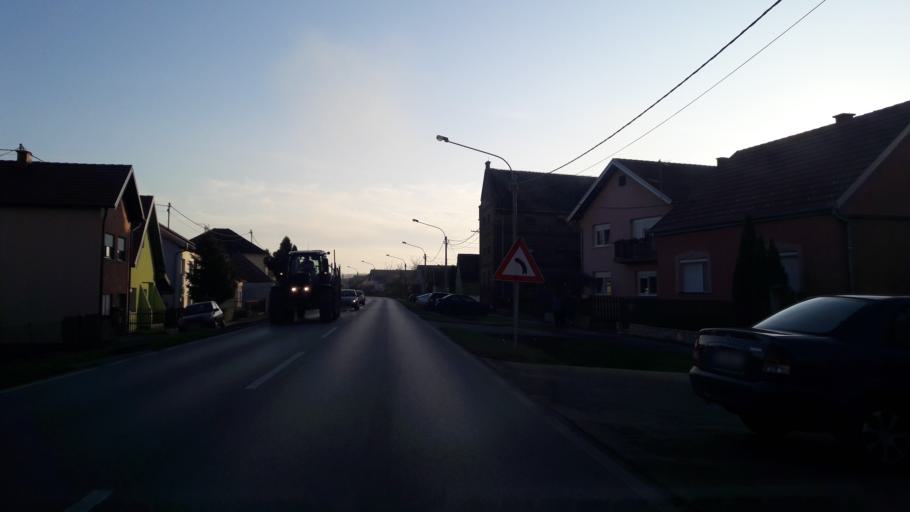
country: HR
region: Osjecko-Baranjska
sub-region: Grad Osijek
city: Bilje
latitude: 45.6003
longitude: 18.7432
